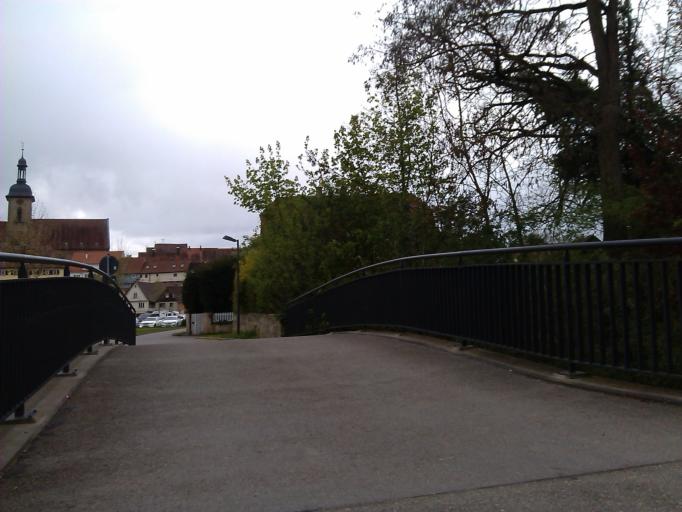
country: DE
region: Baden-Wuerttemberg
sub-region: Regierungsbezirk Stuttgart
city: Lauffen am Neckar
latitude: 49.0783
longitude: 9.1538
